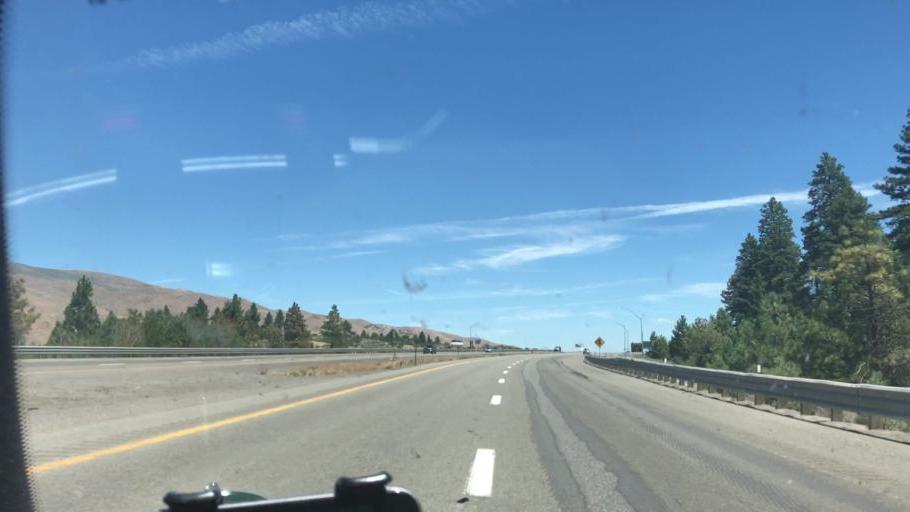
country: US
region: Nevada
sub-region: Washoe County
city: Verdi
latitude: 39.5124
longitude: -119.9909
